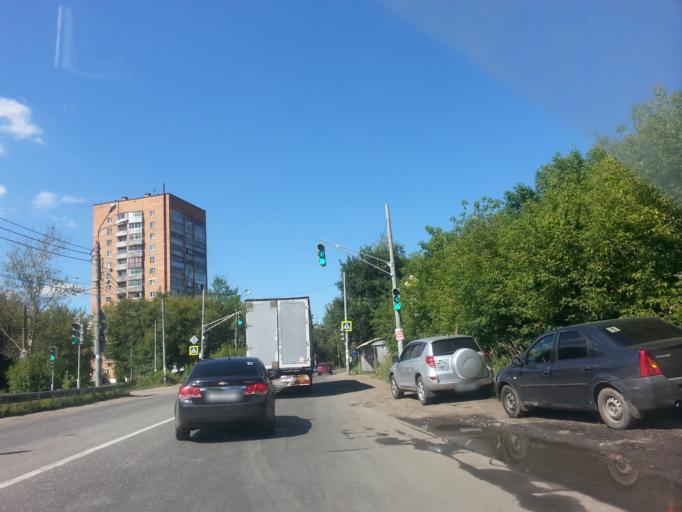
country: RU
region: Nizjnij Novgorod
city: Gorbatovka
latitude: 56.3349
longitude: 43.8496
